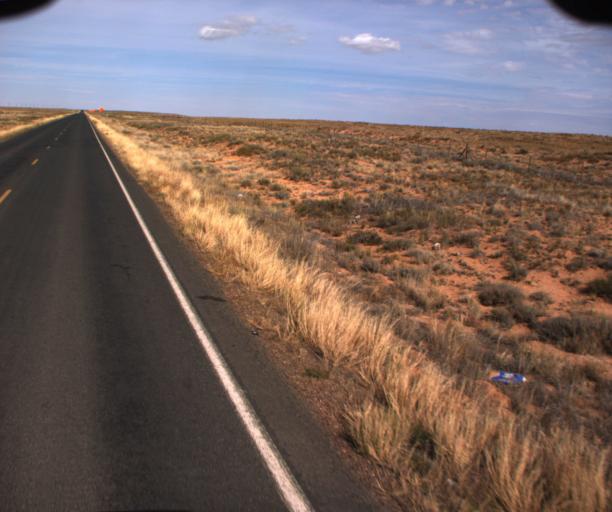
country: US
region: Arizona
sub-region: Apache County
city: Chinle
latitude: 35.9964
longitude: -109.6023
